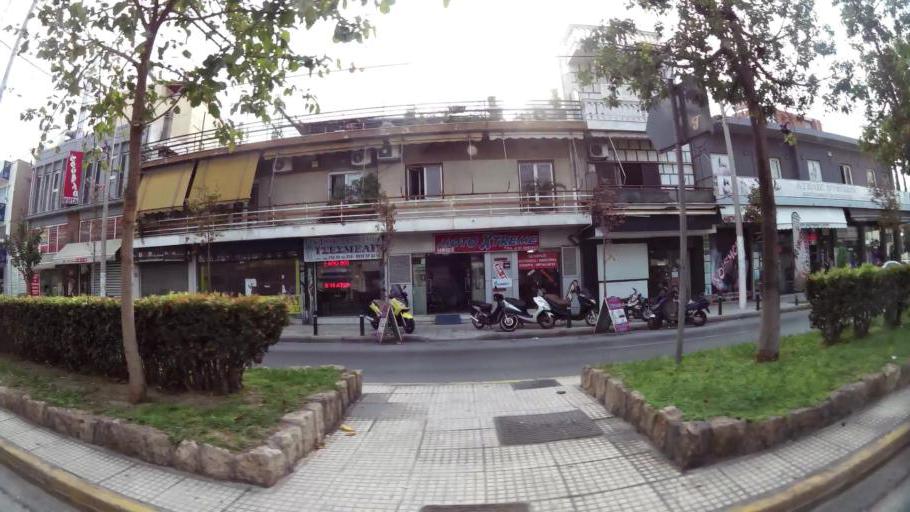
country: GR
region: Attica
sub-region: Nomarchia Athinas
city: Peristeri
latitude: 38.0004
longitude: 23.6846
